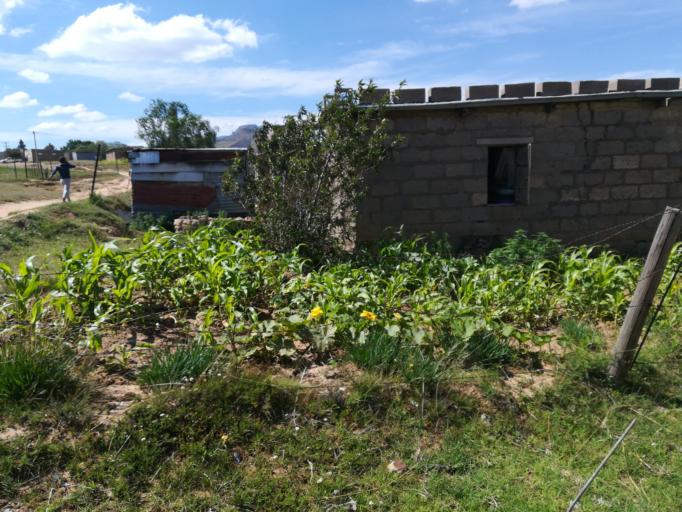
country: LS
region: Mohale's Hoek District
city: Mohale's Hoek
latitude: -30.1031
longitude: 27.4698
